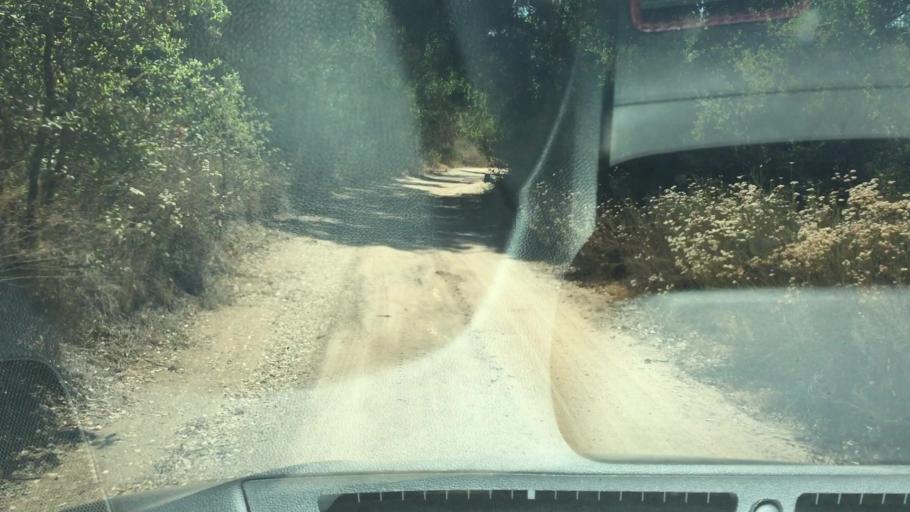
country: US
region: California
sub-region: San Diego County
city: Alpine
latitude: 32.7560
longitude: -116.7474
